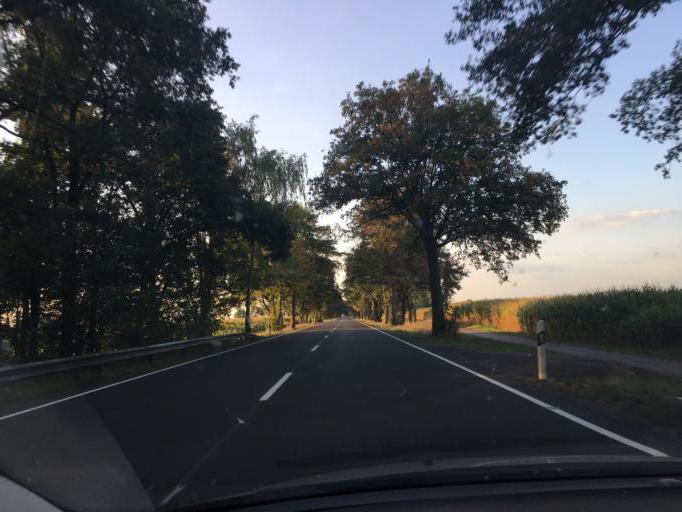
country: DE
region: Lower Saxony
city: Bergen
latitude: 52.7851
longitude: 9.9743
